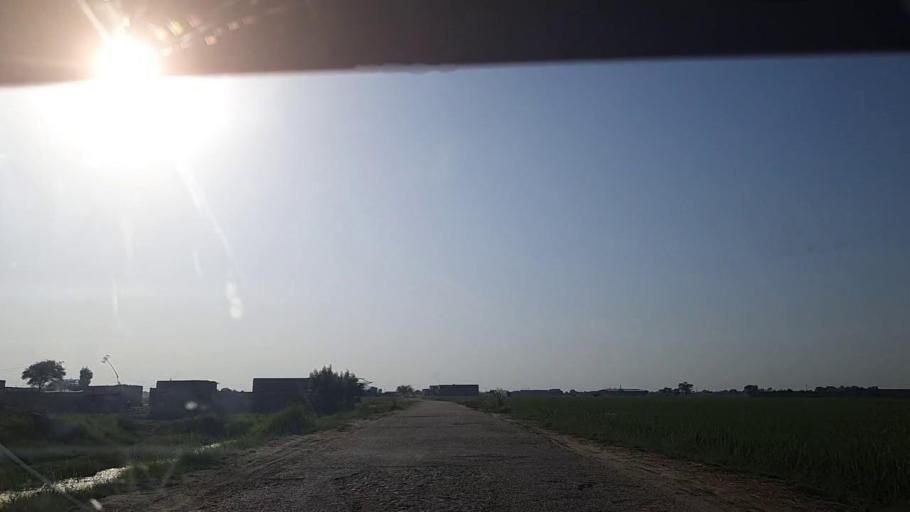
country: PK
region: Sindh
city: Tangwani
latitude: 28.2602
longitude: 69.0114
